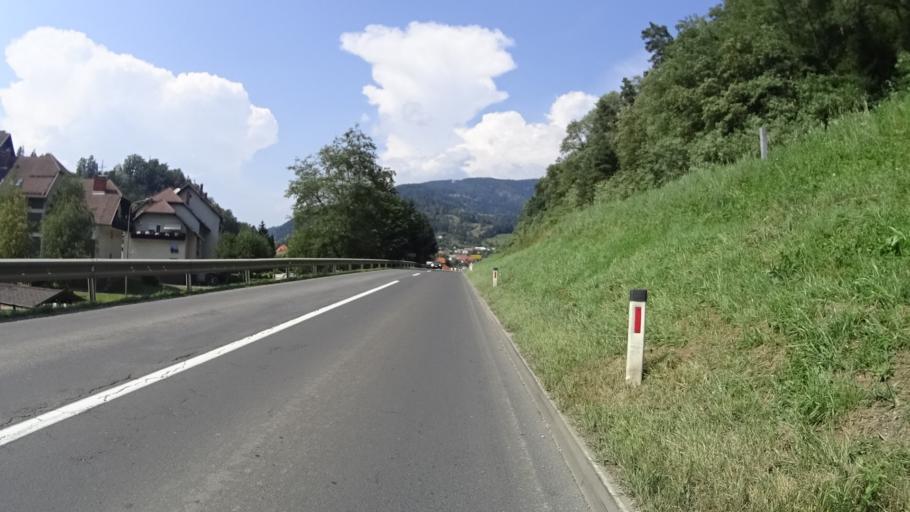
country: SI
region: Dravograd
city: Dravograd
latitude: 46.5812
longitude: 15.0239
